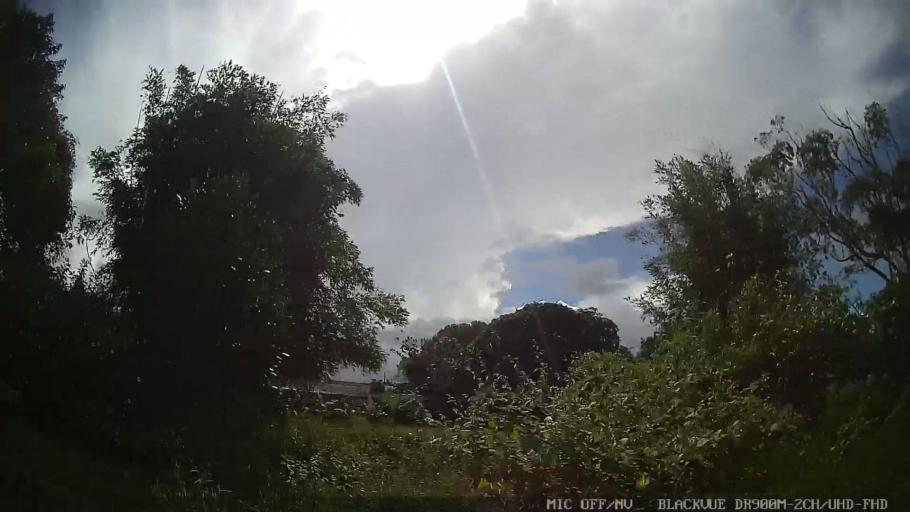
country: BR
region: Sao Paulo
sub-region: Itanhaem
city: Itanhaem
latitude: -24.2371
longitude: -46.8865
